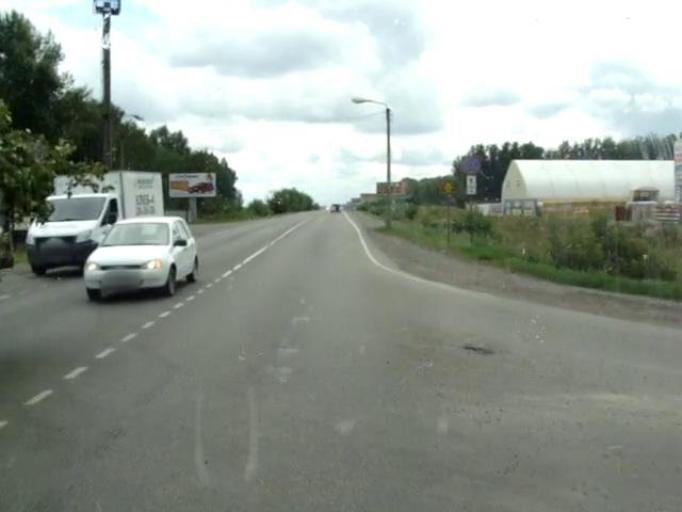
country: RU
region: Altai Krai
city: Zarya
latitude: 52.5750
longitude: 85.1806
